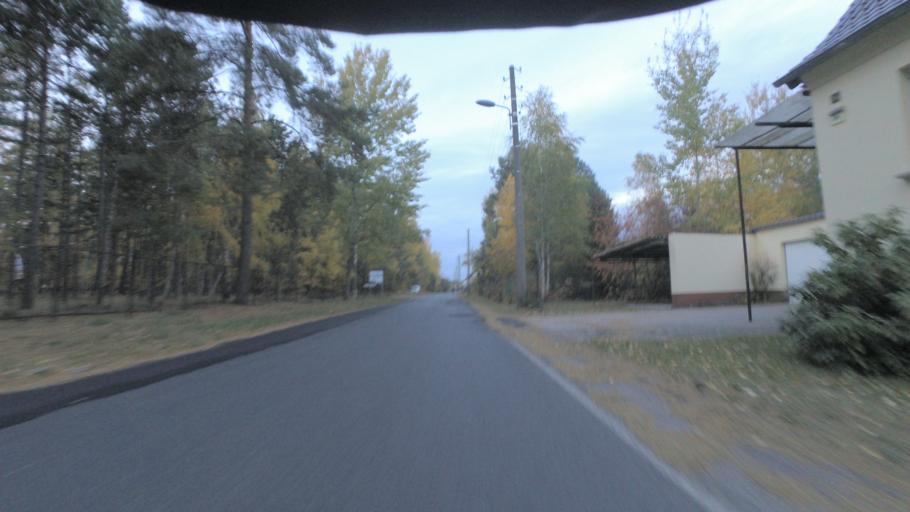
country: DE
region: Brandenburg
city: Sonnewalde
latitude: 51.7686
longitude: 13.6184
